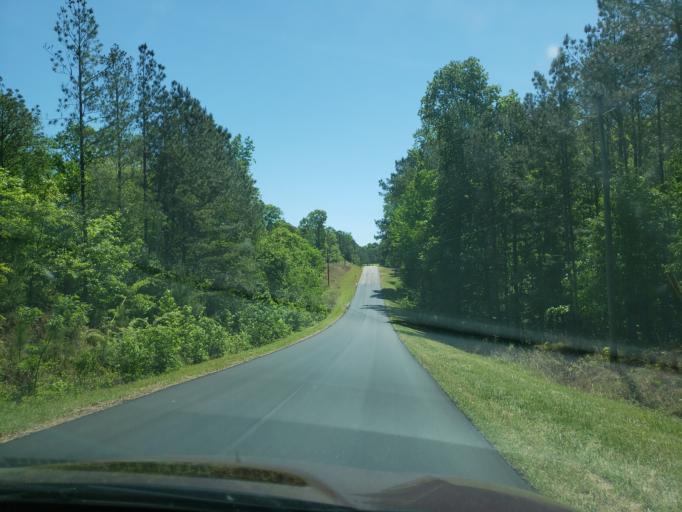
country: US
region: Alabama
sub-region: Tallapoosa County
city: Dadeville
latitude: 32.7005
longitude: -85.8650
